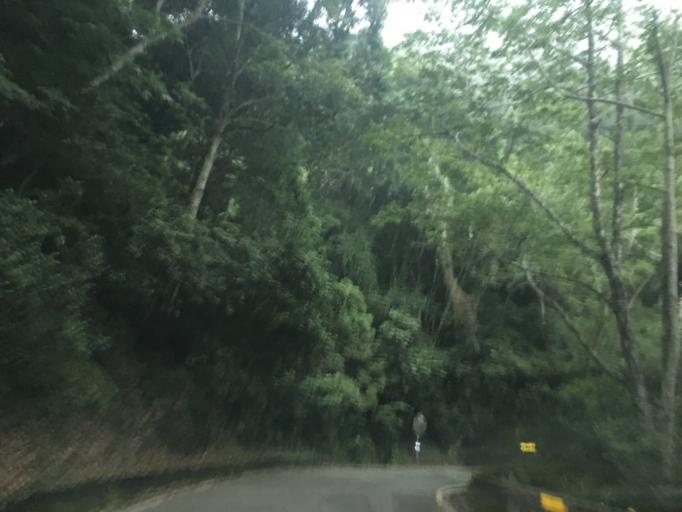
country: TW
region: Taiwan
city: Fengyuan
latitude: 24.2453
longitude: 120.9256
